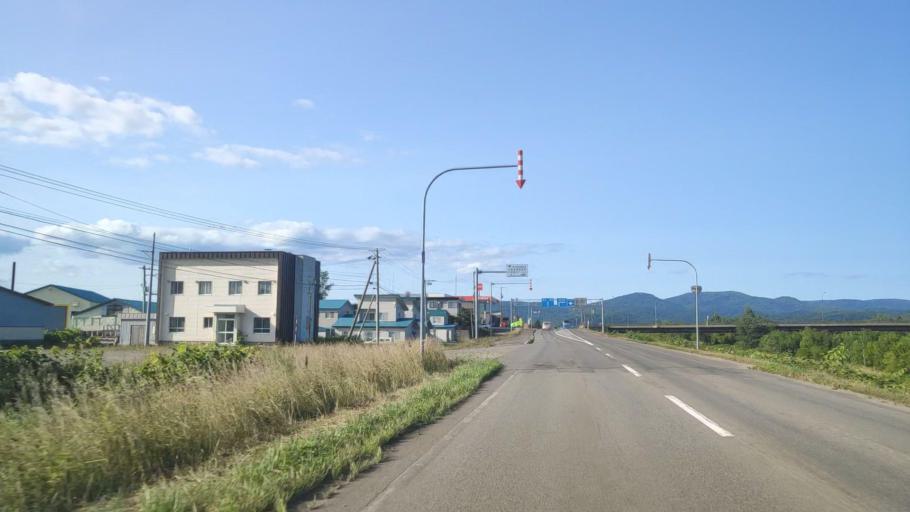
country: JP
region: Hokkaido
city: Makubetsu
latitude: 44.8166
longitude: 142.0670
